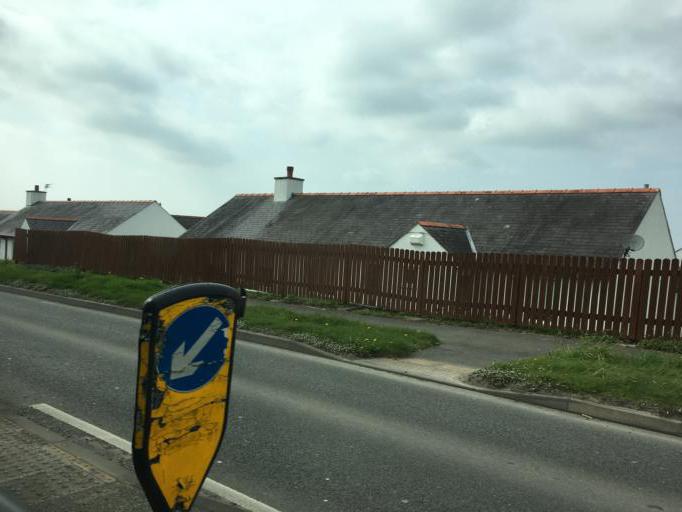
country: GB
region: Wales
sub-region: Gwynedd
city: Caernarfon
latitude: 53.1486
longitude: -4.2663
